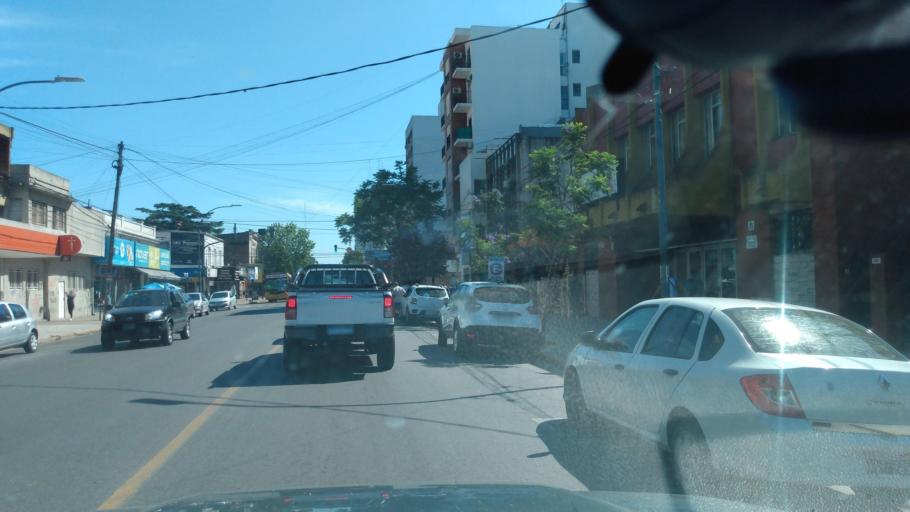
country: AR
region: Buenos Aires
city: Hurlingham
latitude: -34.5403
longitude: -58.7100
